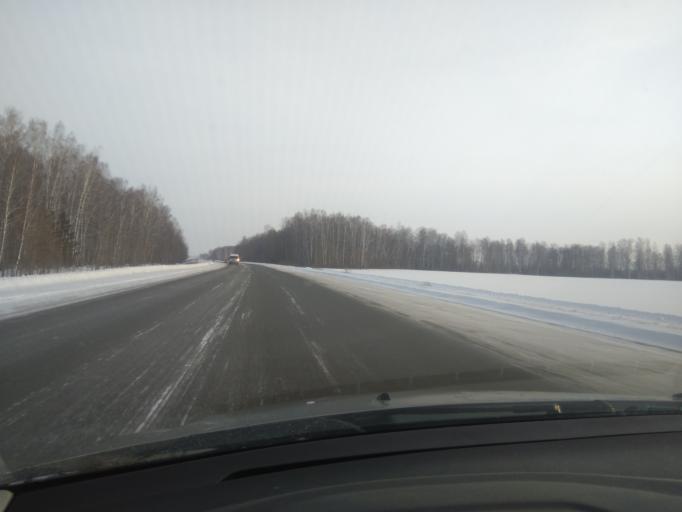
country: RU
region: Sverdlovsk
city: Bogdanovich
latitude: 56.8011
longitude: 62.0185
